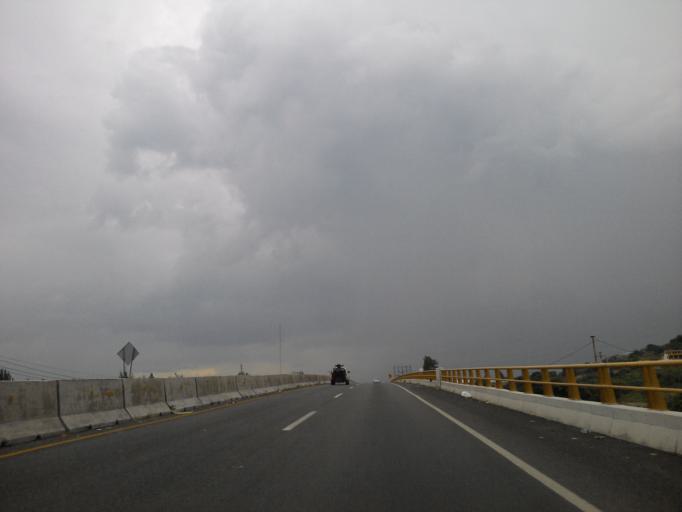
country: MX
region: Jalisco
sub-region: Tonala
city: Paseo Puente Viejo
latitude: 20.5707
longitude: -103.1973
